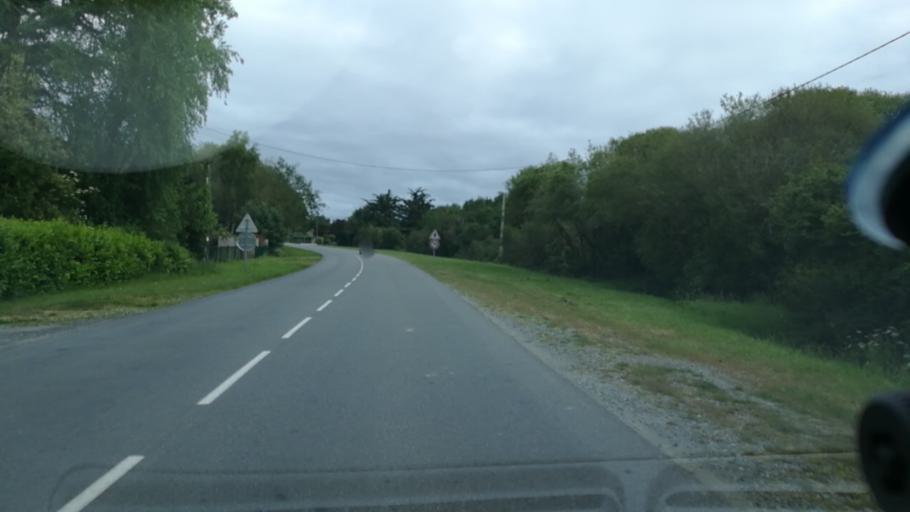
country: FR
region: Brittany
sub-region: Departement du Morbihan
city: Penestin
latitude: 47.4710
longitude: -2.4786
